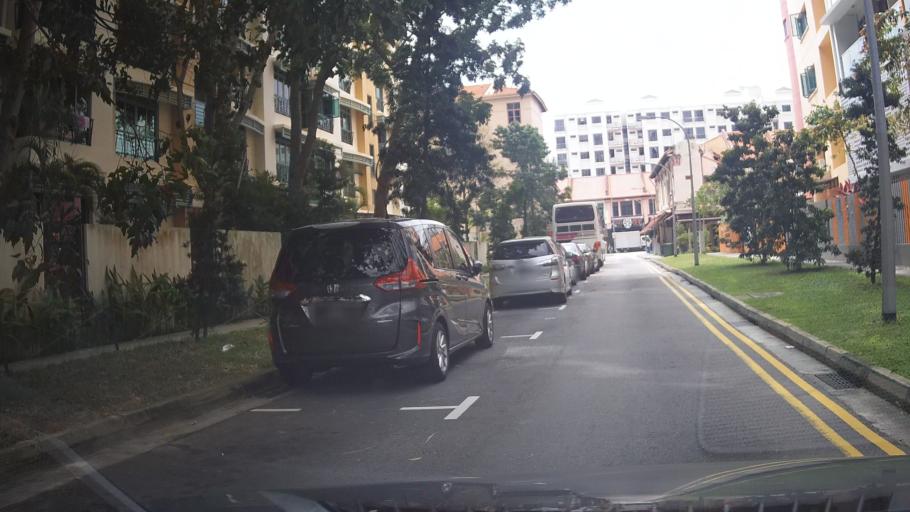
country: SG
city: Singapore
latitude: 1.3158
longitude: 103.8907
